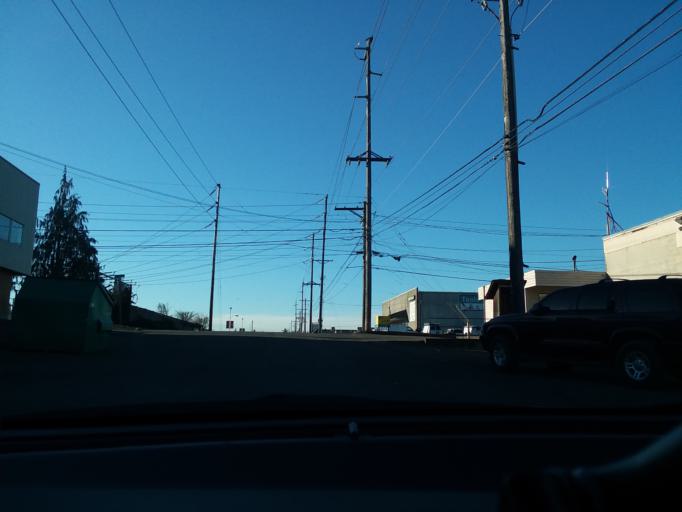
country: US
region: Washington
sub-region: Pierce County
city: Tacoma
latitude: 47.2267
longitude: -122.4764
